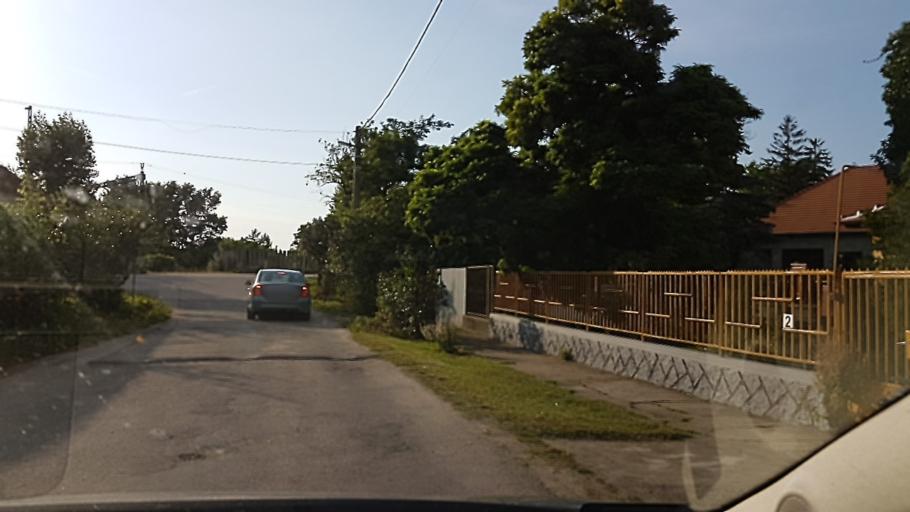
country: HU
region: Pest
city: Dunavarsany
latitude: 47.2511
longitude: 19.0613
